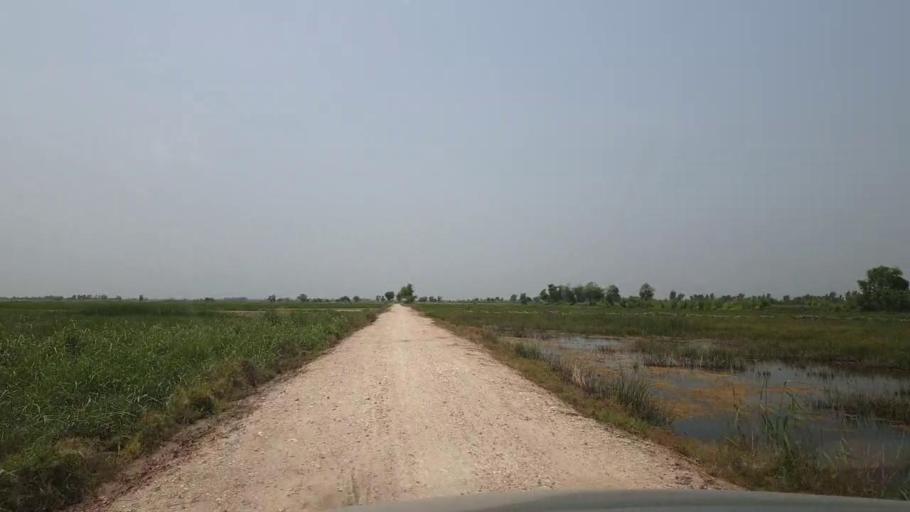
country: PK
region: Sindh
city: Garhi Yasin
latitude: 27.8680
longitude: 68.4875
